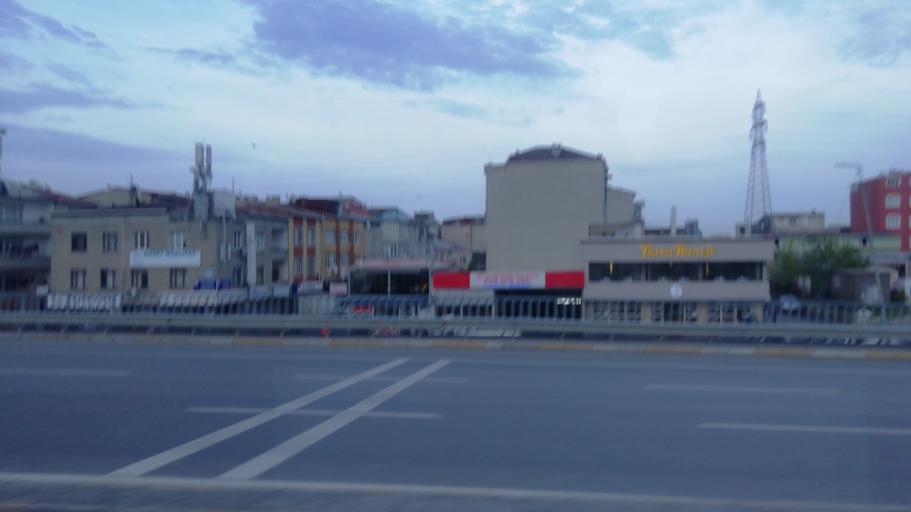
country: TR
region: Istanbul
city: Mahmutbey
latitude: 41.0525
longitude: 28.7926
